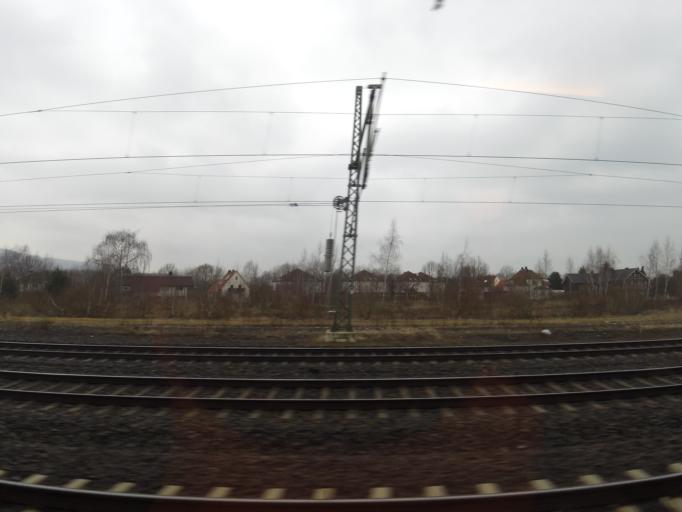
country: DE
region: North Rhine-Westphalia
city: Porta Westfalica
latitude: 52.2572
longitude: 8.9296
